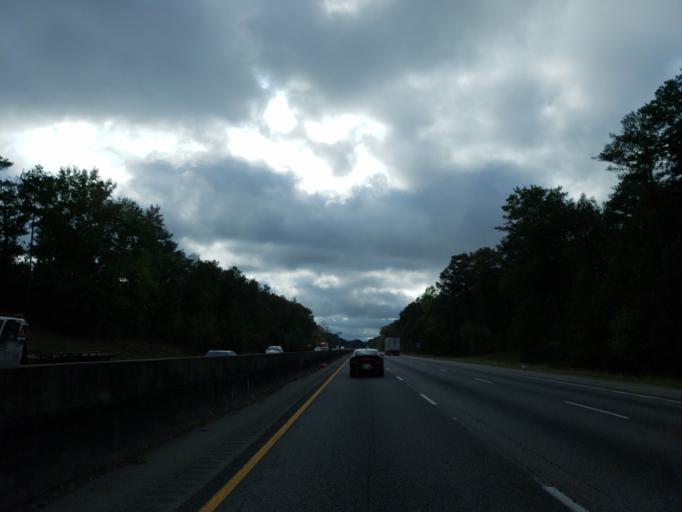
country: US
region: Alabama
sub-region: Saint Clair County
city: Moody
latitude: 33.5772
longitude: -86.4759
